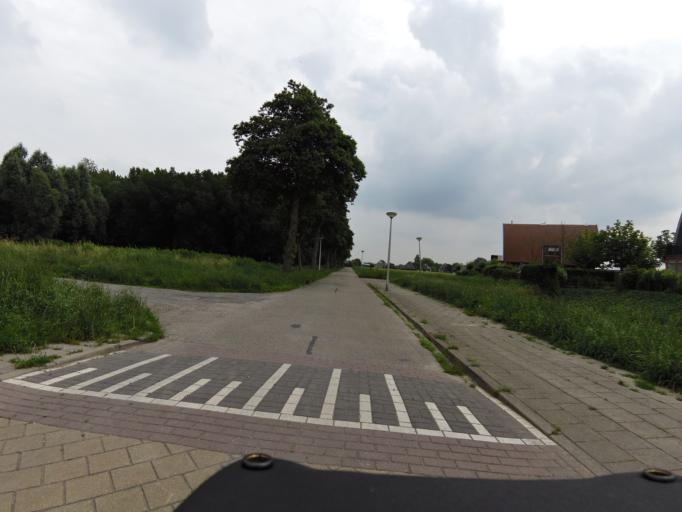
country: NL
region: South Holland
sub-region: Gemeente Hellevoetsluis
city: Nieuwenhoorn
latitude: 51.8542
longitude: 4.1485
